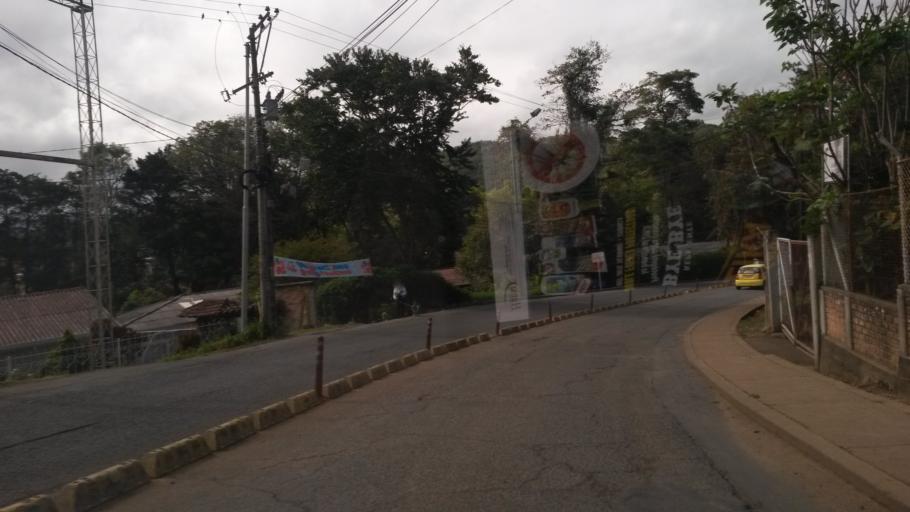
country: CO
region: Cauca
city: Popayan
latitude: 2.4742
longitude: -76.5781
